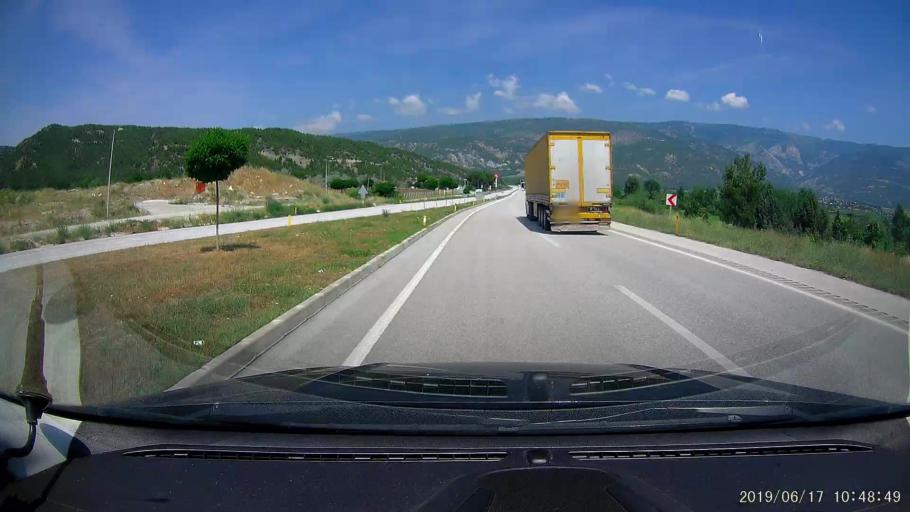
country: TR
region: Corum
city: Hacihamza
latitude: 41.0935
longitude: 34.4221
